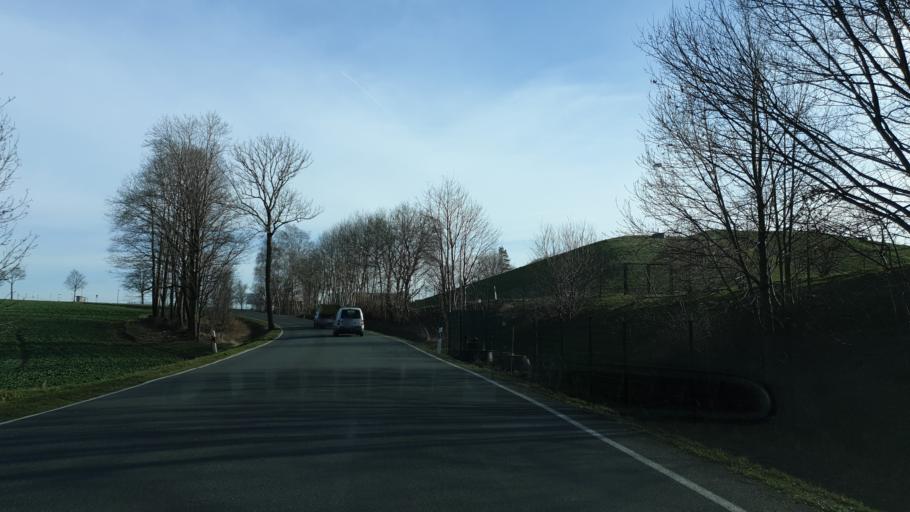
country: DE
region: Saxony
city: Zwonitz
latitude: 50.6450
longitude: 12.7824
